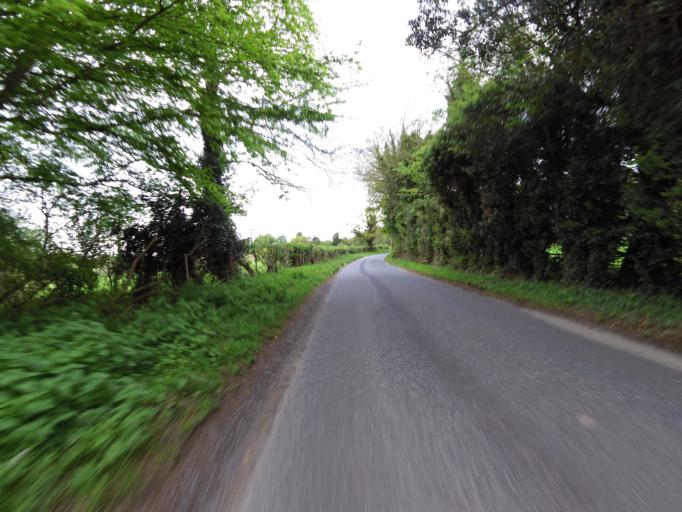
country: GB
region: England
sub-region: Suffolk
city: Kesgrave
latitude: 52.0087
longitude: 1.2433
